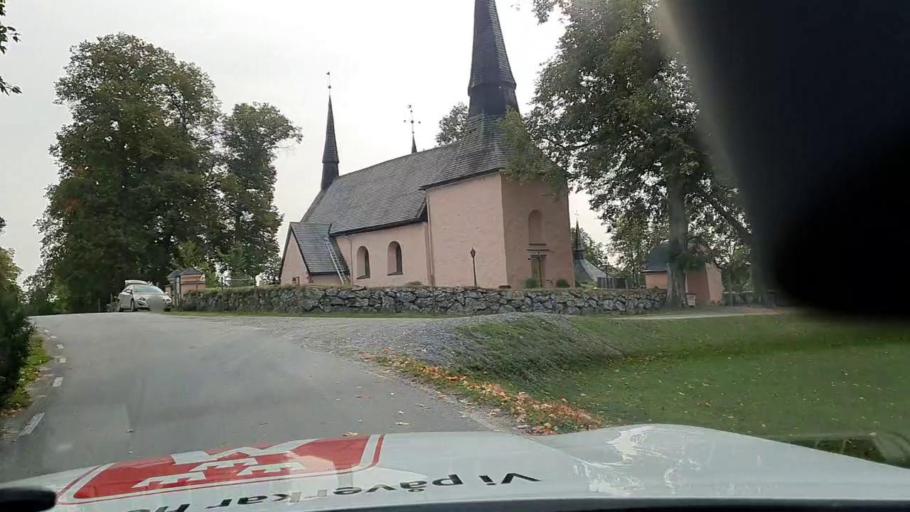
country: SE
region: Soedermanland
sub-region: Nykopings Kommun
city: Stigtomta
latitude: 58.9824
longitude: 16.9310
